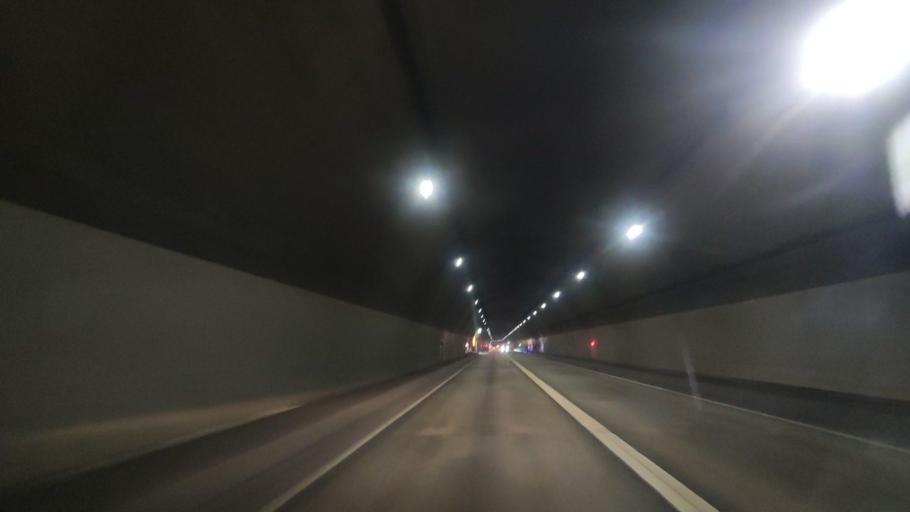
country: JP
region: Nagano
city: Okaya
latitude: 36.0921
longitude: 138.0762
